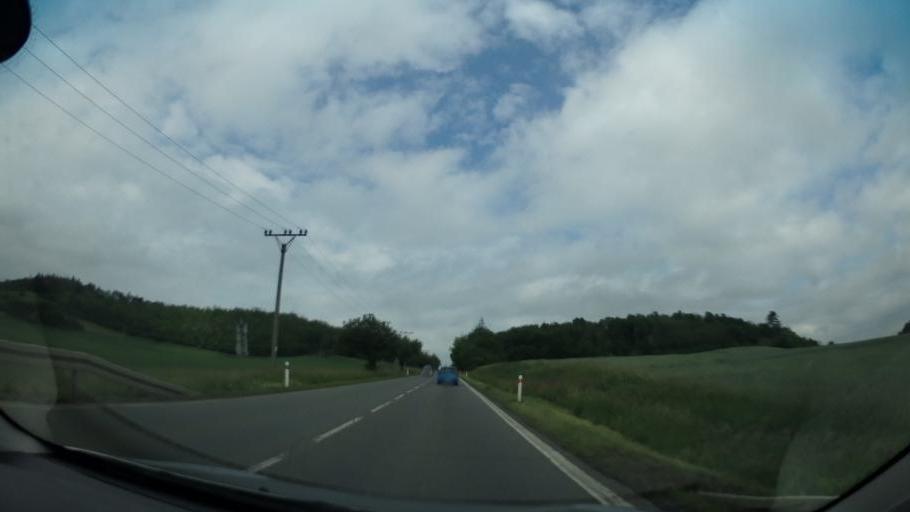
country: CZ
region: South Moravian
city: Cebin
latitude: 49.3076
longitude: 16.5025
